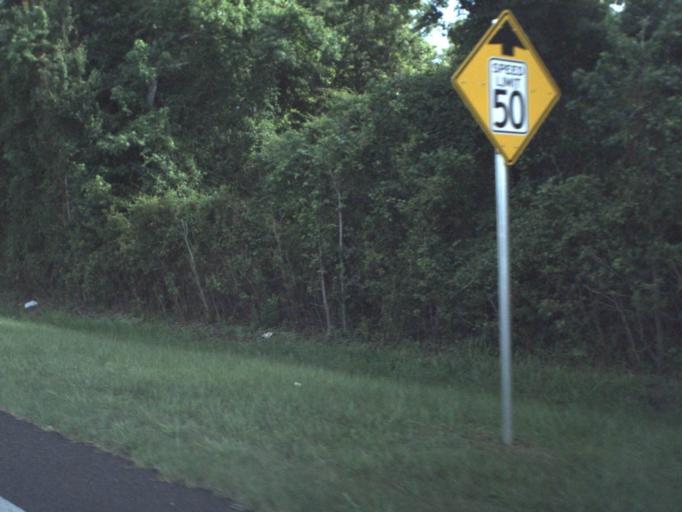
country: US
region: Florida
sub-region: Alachua County
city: Alachua
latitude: 29.7397
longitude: -82.3843
